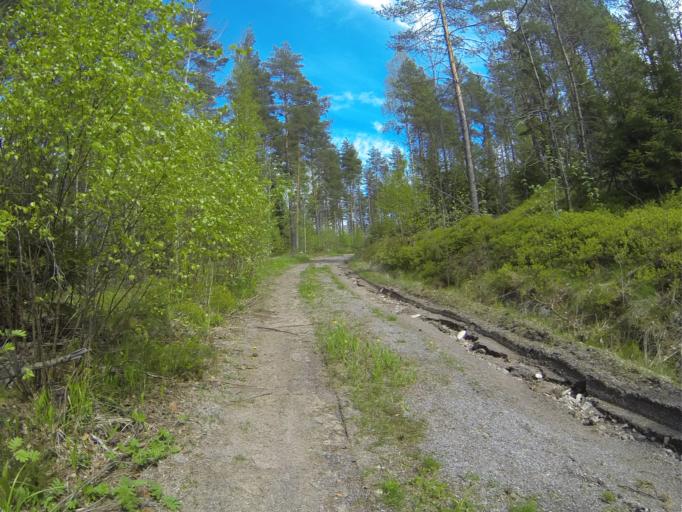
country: FI
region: Varsinais-Suomi
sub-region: Salo
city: Halikko
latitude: 60.3387
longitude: 23.0829
